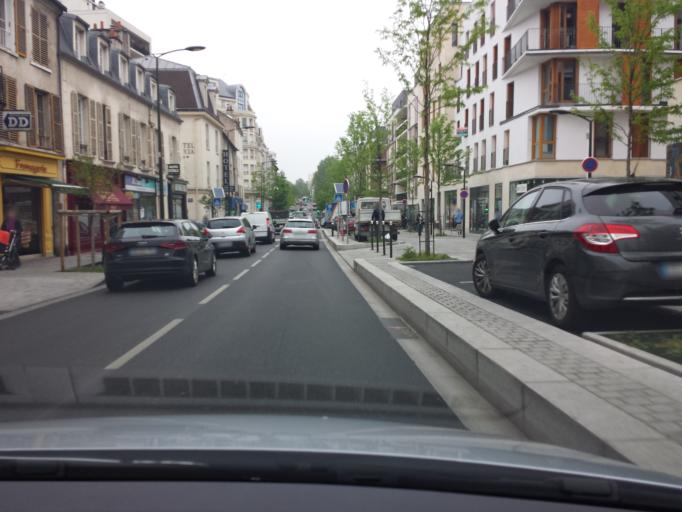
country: FR
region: Ile-de-France
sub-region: Departement des Hauts-de-Seine
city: Bourg-la-Reine
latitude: 48.7803
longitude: 2.3157
